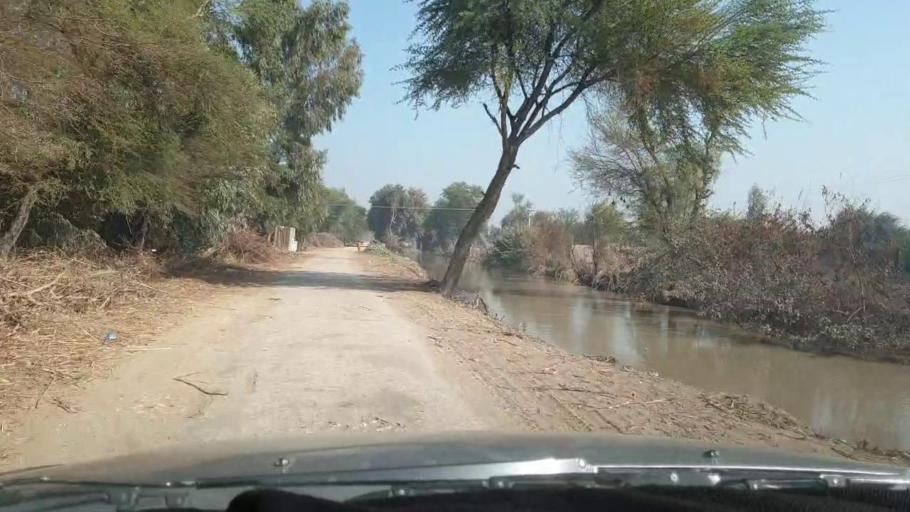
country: PK
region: Sindh
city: Khanpur
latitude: 27.7839
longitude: 69.5482
